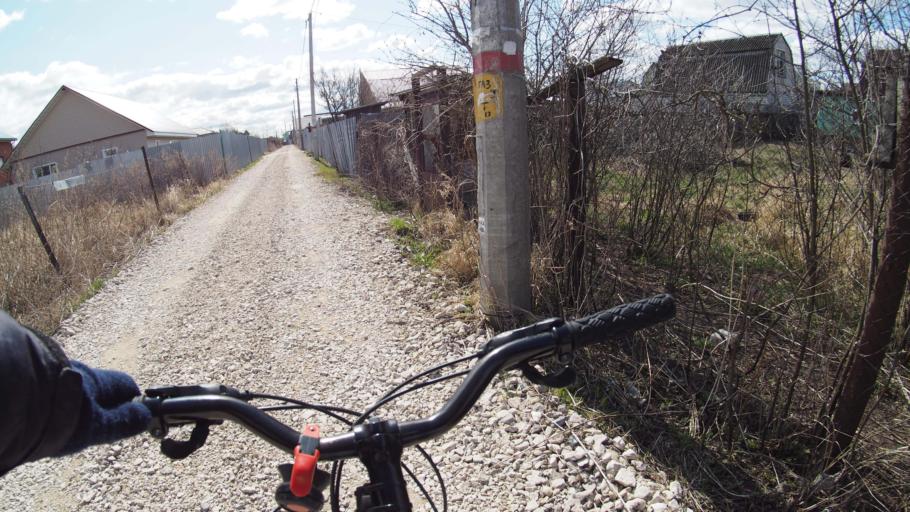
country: RU
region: Moskovskaya
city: Malyshevo
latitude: 55.5486
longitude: 38.3172
